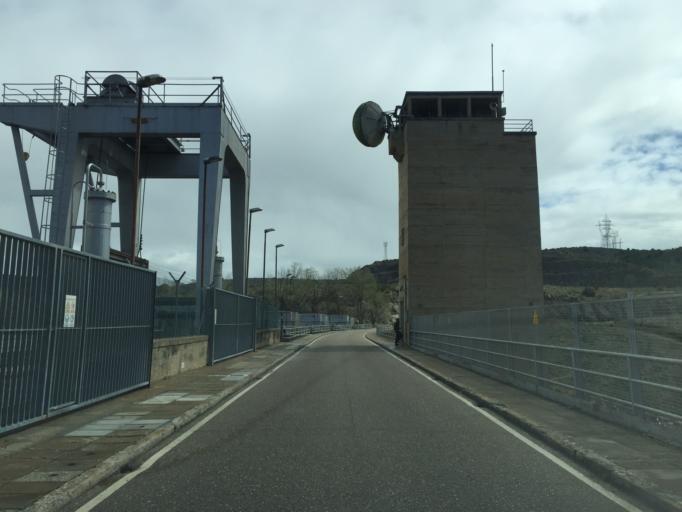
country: ES
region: Castille and Leon
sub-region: Provincia de Zamora
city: Moral de Sayago
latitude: 41.4914
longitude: -6.0862
